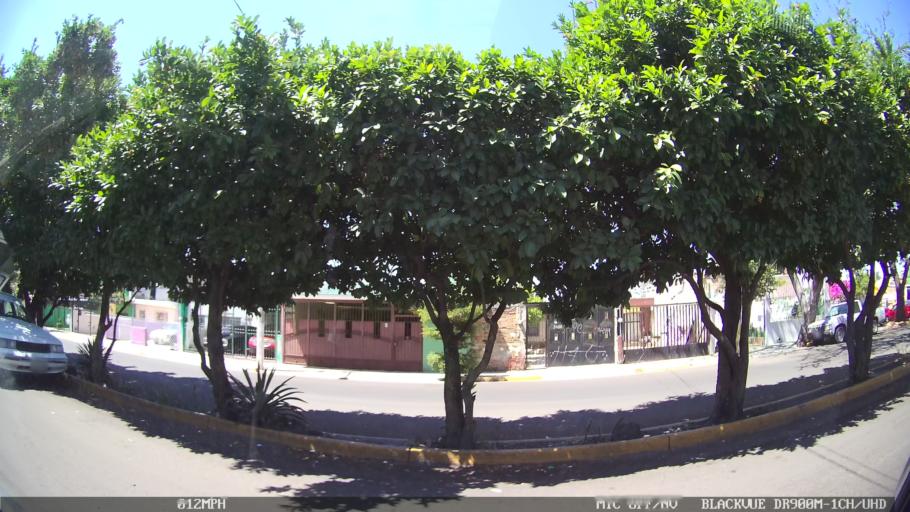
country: MX
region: Jalisco
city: Tlaquepaque
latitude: 20.6877
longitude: -103.2896
